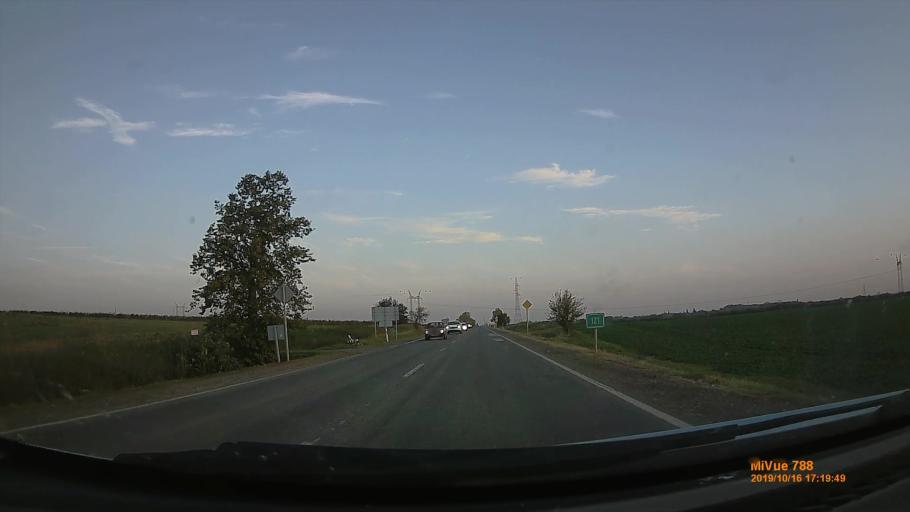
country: HU
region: Heves
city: Kerecsend
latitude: 47.7831
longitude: 20.3633
